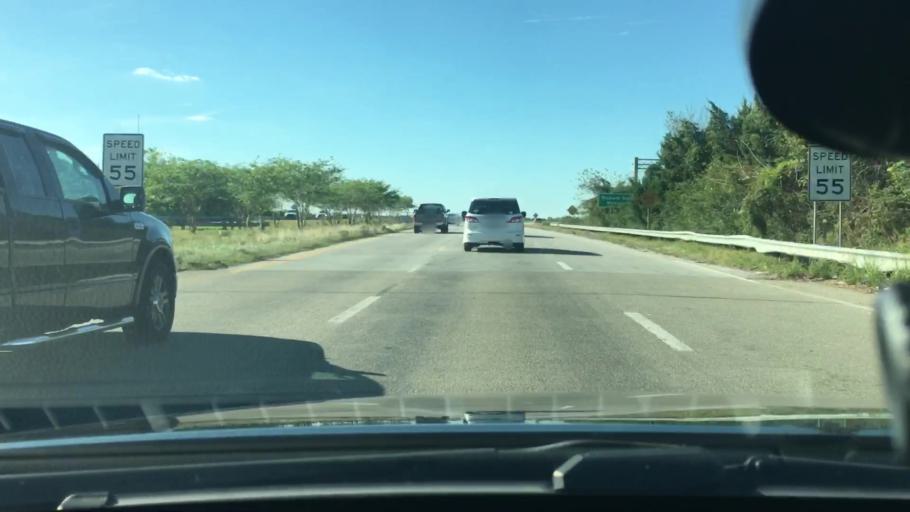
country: US
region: North Carolina
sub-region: Craven County
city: James City
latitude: 35.0945
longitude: -77.0410
